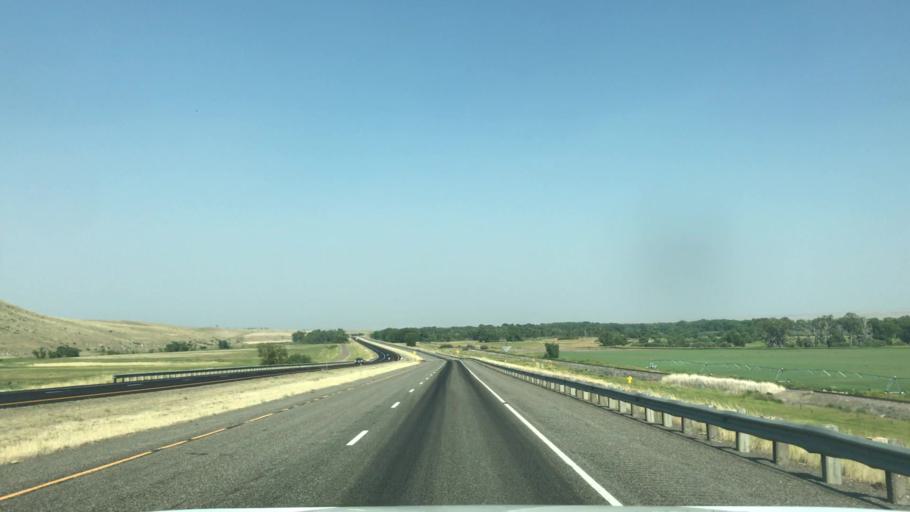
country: US
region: Montana
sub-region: Cascade County
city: Sun Prairie
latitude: 47.2295
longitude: -111.7606
